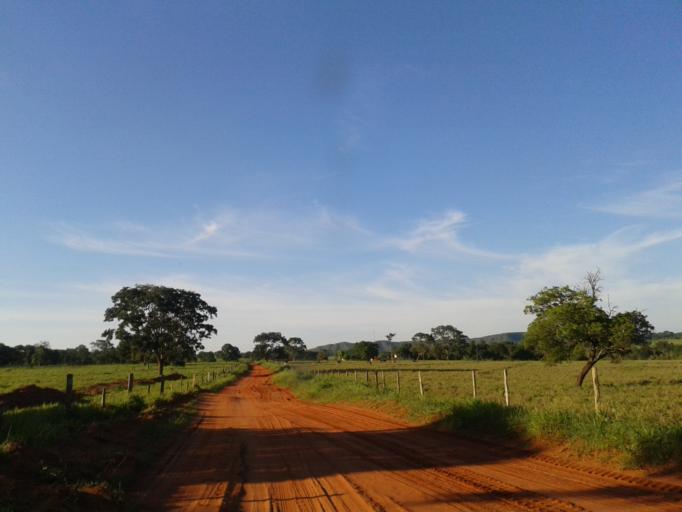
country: BR
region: Minas Gerais
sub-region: Santa Vitoria
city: Santa Vitoria
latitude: -18.9553
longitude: -49.8638
